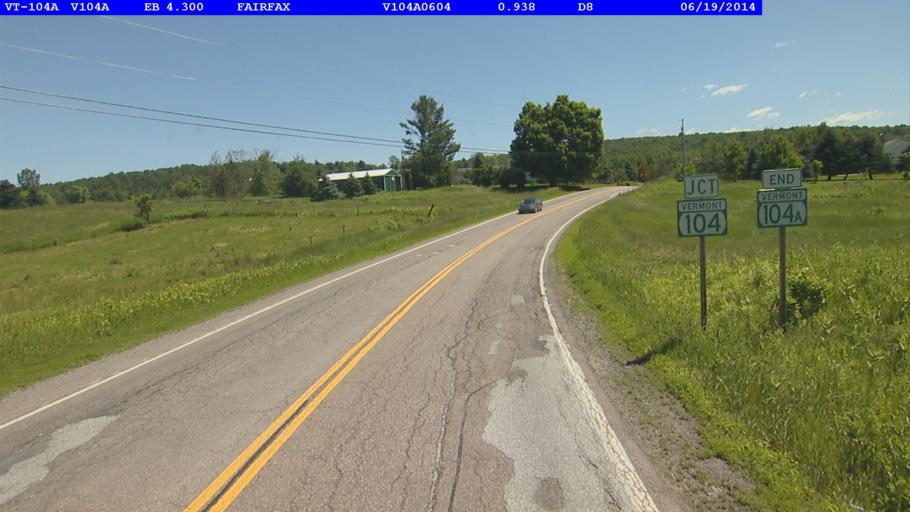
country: US
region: Vermont
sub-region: Chittenden County
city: Milton
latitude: 44.6835
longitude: -73.0338
